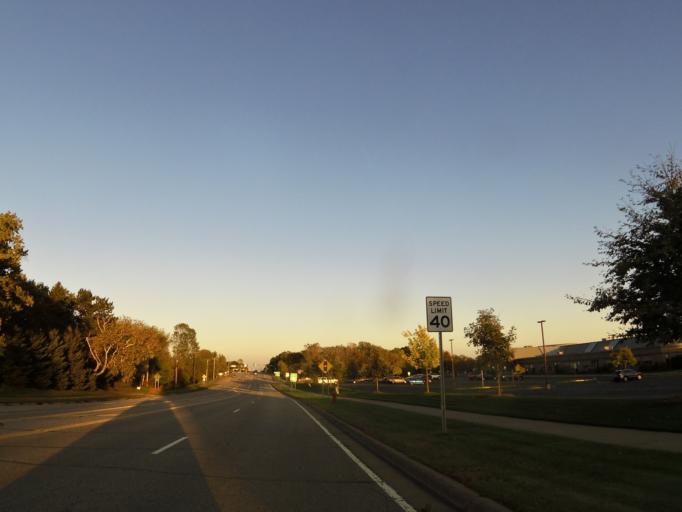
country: US
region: Minnesota
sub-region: Dakota County
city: Inver Grove Heights
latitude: 44.8333
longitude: -93.0661
